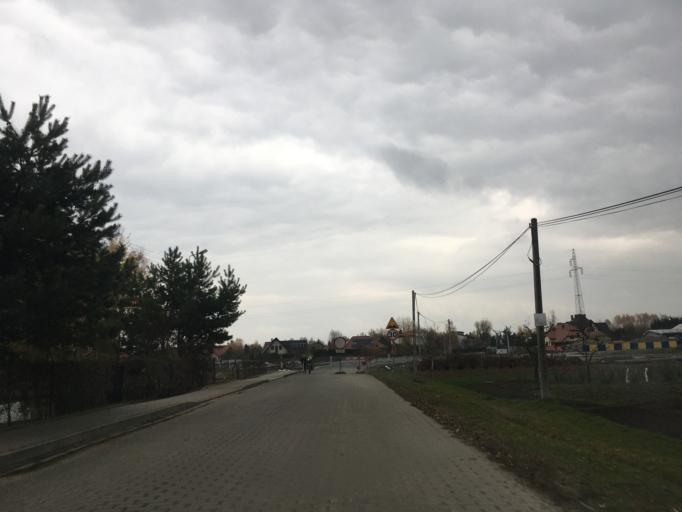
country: PL
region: Masovian Voivodeship
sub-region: Powiat piaseczynski
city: Lesznowola
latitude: 52.0464
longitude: 20.9330
